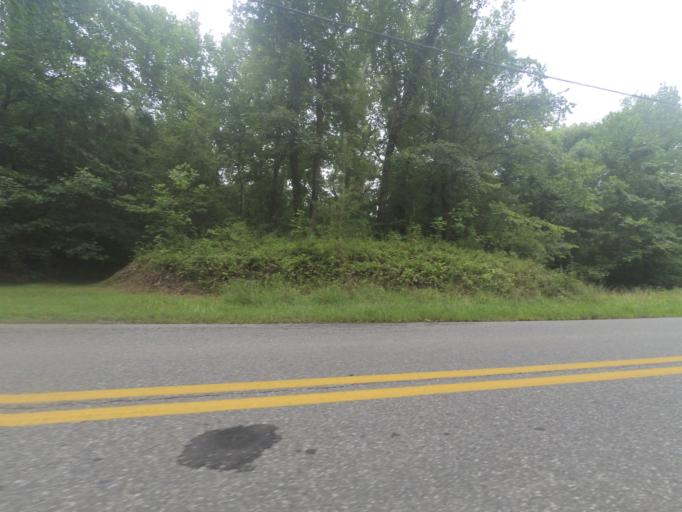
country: US
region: West Virginia
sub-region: Cabell County
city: Huntington
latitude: 38.4030
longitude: -82.3959
